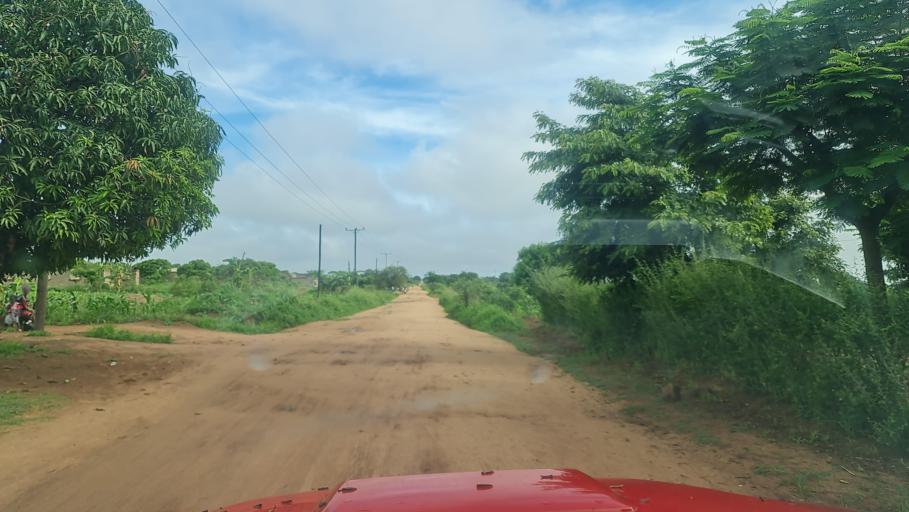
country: MW
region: Southern Region
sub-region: Nsanje District
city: Nsanje
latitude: -17.3147
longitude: 35.5924
